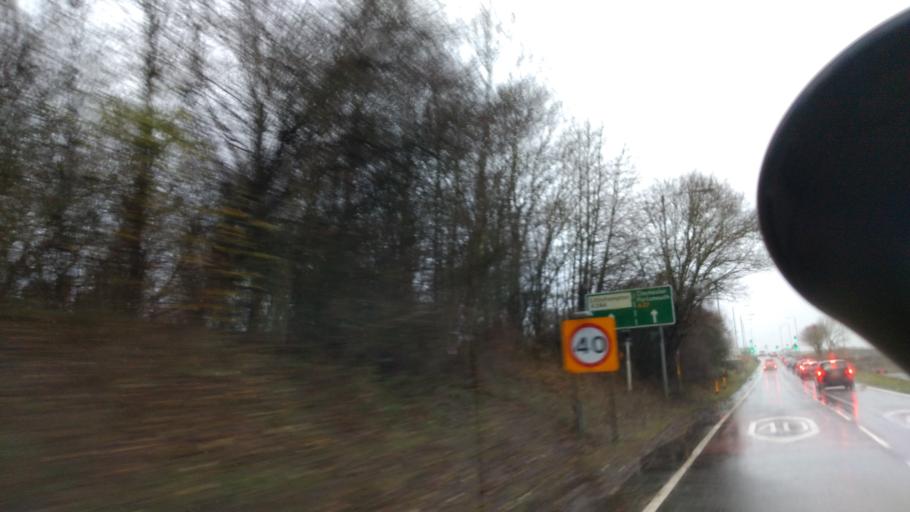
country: GB
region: England
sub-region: West Sussex
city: Arundel
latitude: 50.8428
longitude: -0.5369
